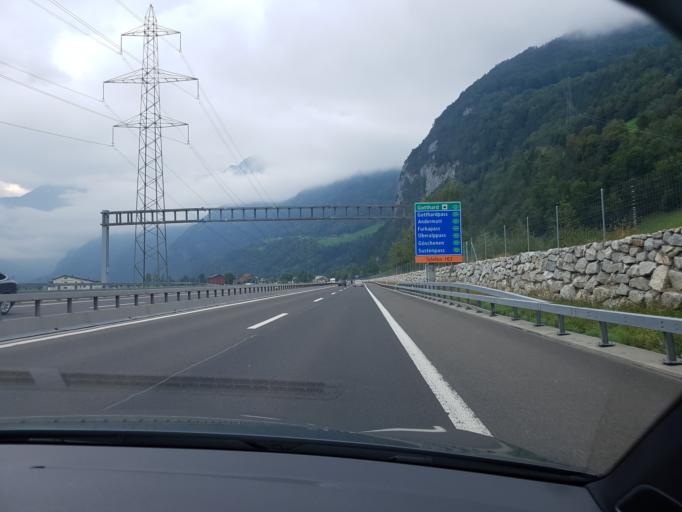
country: CH
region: Uri
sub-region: Uri
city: Attinghausen
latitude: 46.8549
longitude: 8.6337
